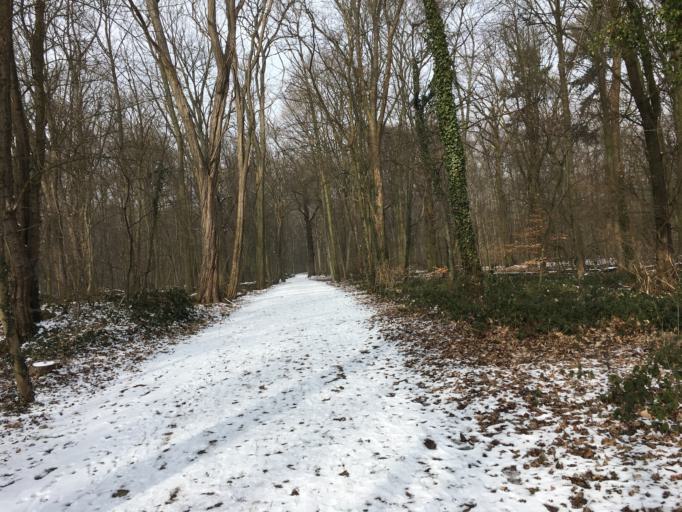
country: DE
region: North Rhine-Westphalia
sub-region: Regierungsbezirk Koln
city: Kreuzau
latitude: 50.7694
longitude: 6.4980
